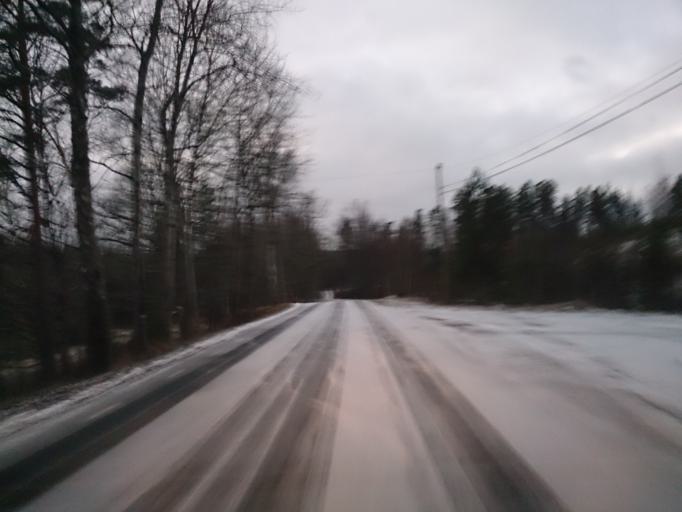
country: SE
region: OEstergoetland
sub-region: Atvidabergs Kommun
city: Atvidaberg
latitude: 58.2774
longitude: 16.1735
